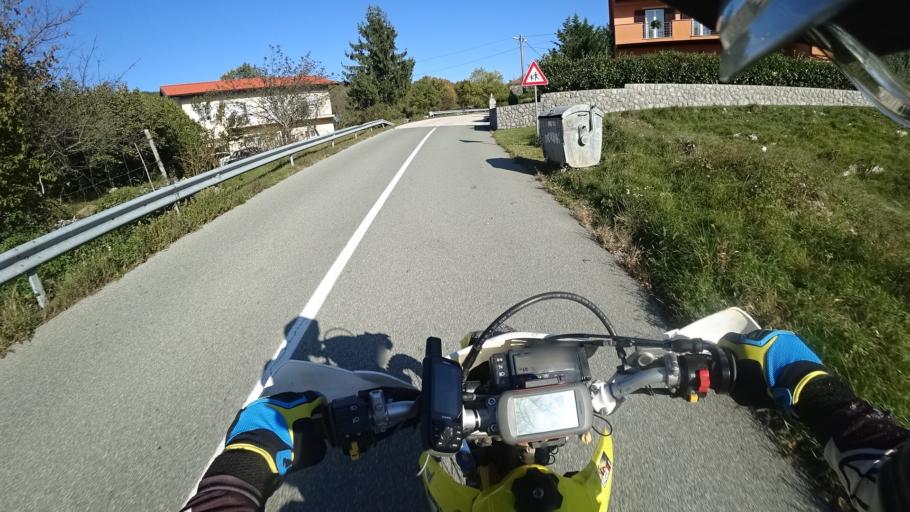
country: HR
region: Primorsko-Goranska
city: Klana
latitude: 45.4450
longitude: 14.3330
